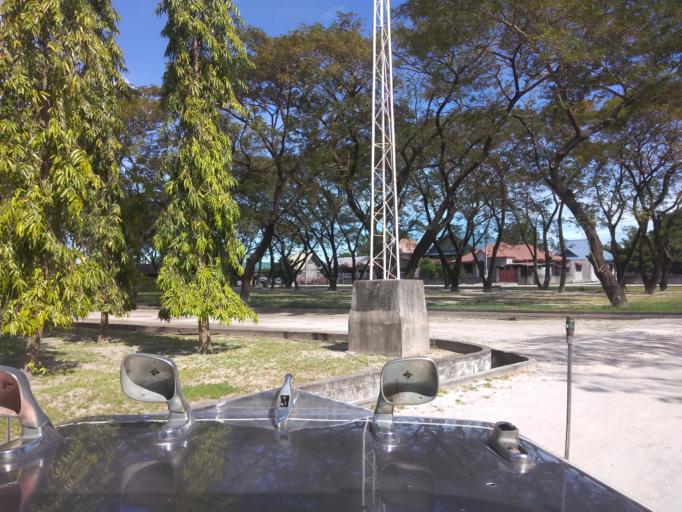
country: PH
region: Central Luzon
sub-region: Province of Pampanga
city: Magliman
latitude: 15.0335
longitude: 120.6358
